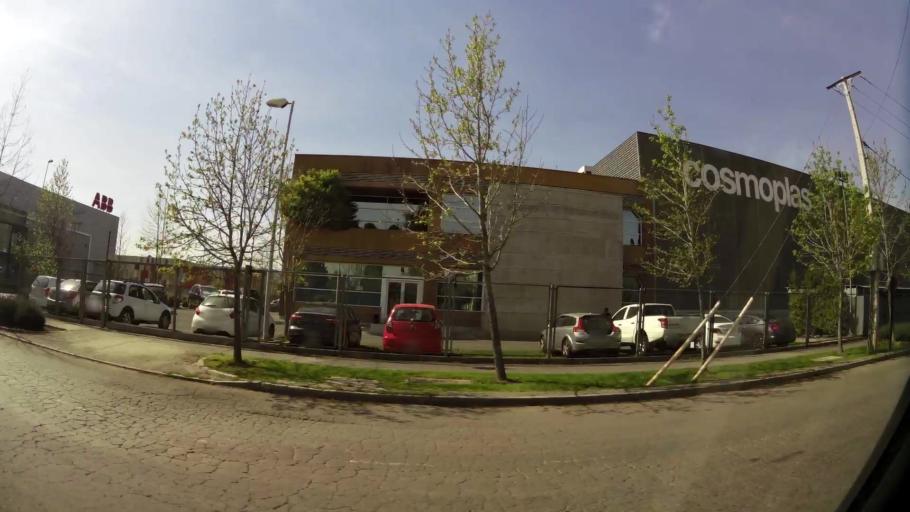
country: CL
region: Santiago Metropolitan
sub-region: Provincia de Santiago
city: Lo Prado
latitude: -33.4297
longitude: -70.7794
